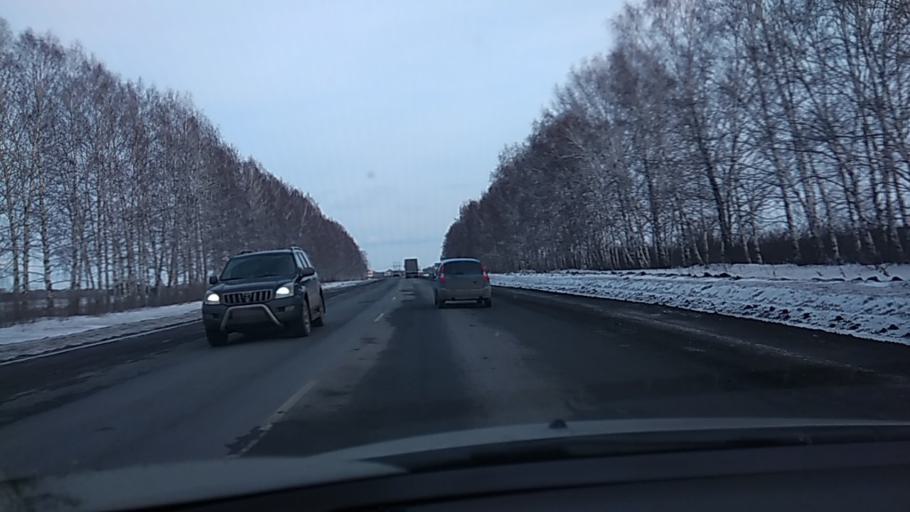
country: RU
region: Sverdlovsk
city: Pokrovskoye
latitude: 56.4657
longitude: 61.6856
